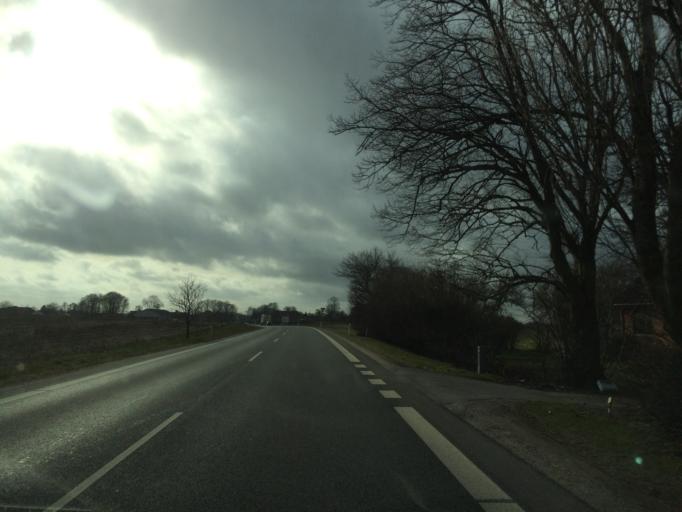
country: DK
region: Central Jutland
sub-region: Favrskov Kommune
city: Ulstrup
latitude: 56.5006
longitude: 9.7666
